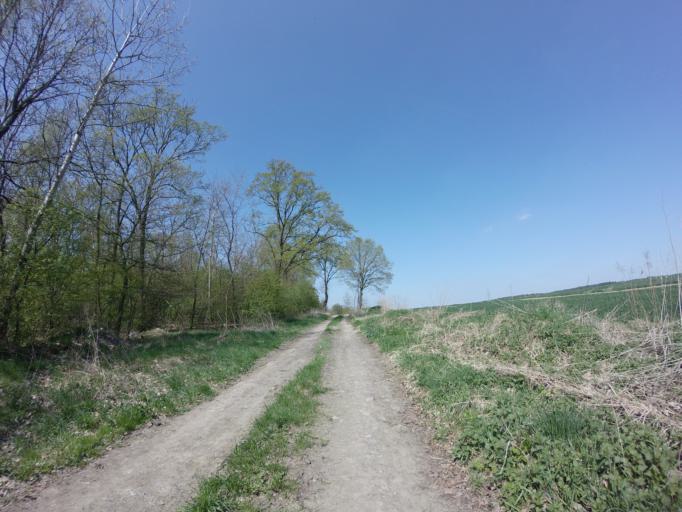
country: PL
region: West Pomeranian Voivodeship
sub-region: Powiat choszczenski
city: Choszczno
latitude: 53.2058
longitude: 15.3633
